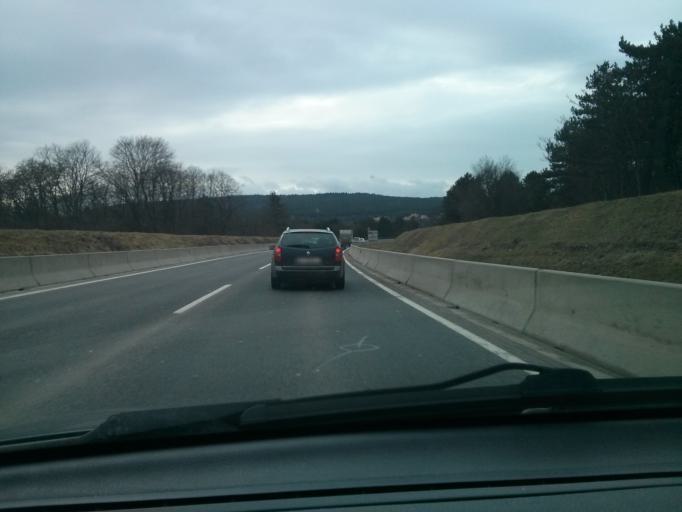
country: AT
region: Lower Austria
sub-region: Politischer Bezirk Wiener Neustadt
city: Theresienfeld
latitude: 47.8490
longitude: 16.1984
